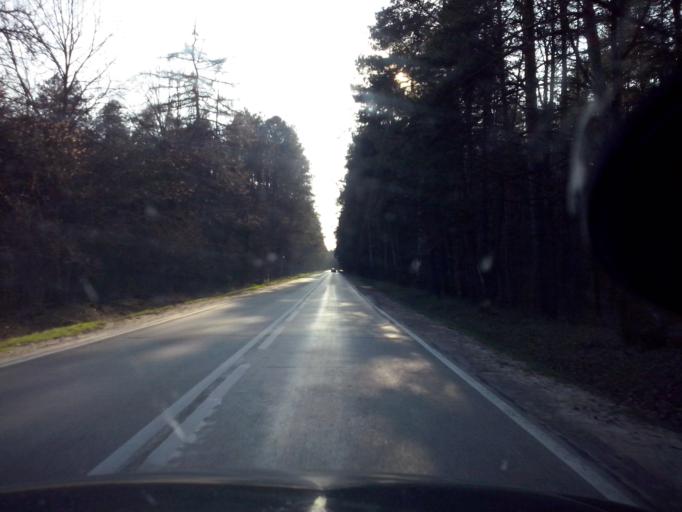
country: PL
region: Lublin Voivodeship
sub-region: Powiat janowski
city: Potok Wielki
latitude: 50.7459
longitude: 22.2238
